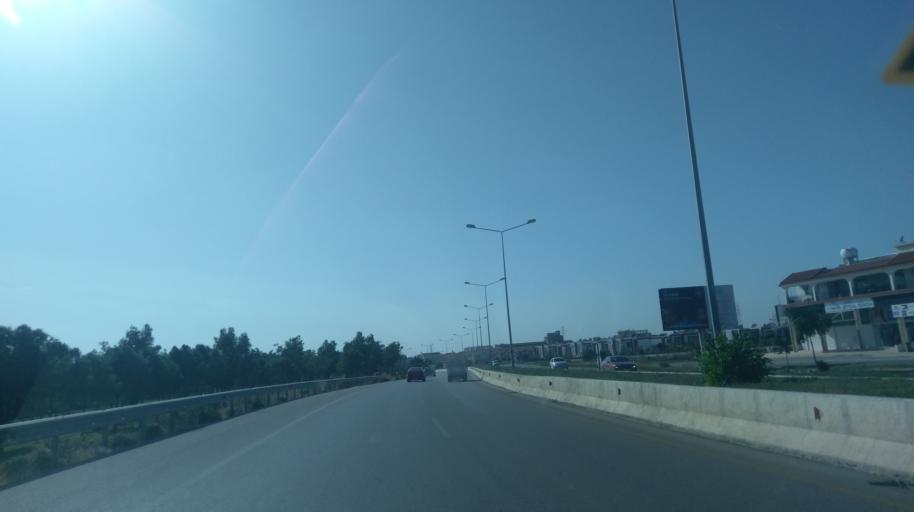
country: CY
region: Ammochostos
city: Trikomo
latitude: 35.2000
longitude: 33.8945
